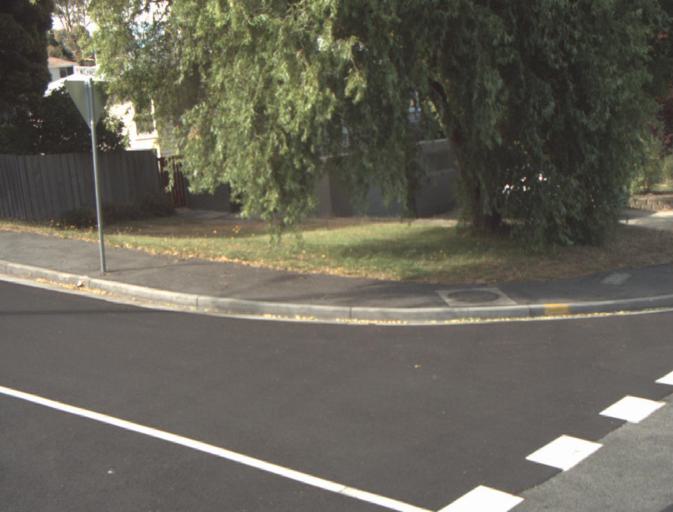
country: AU
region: Tasmania
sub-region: Launceston
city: Summerhill
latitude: -41.4601
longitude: 147.1278
